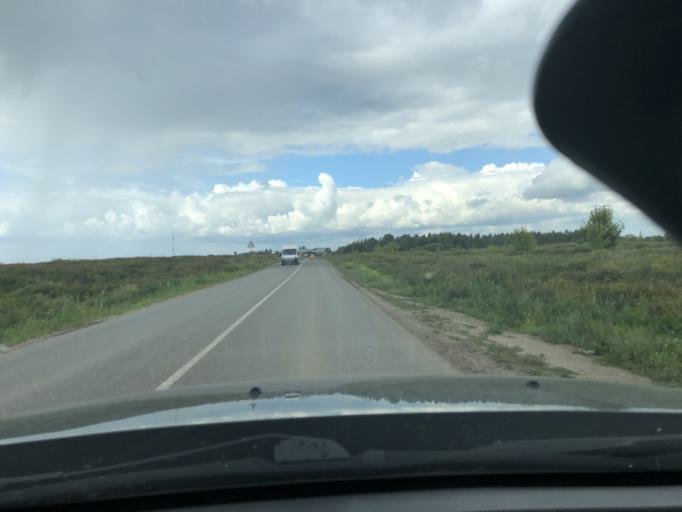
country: RU
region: Tula
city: Kamenetskiy
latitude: 54.0131
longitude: 38.2510
